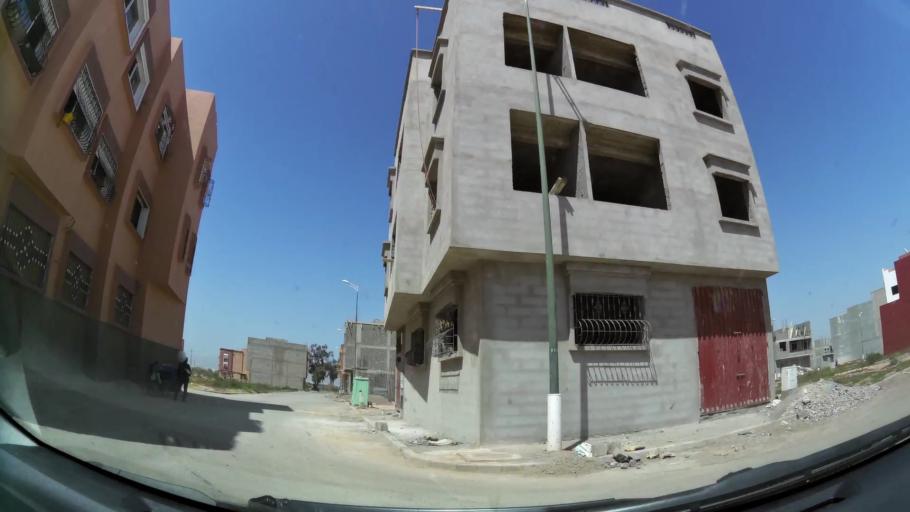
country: MA
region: Souss-Massa-Draa
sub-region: Inezgane-Ait Mellou
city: Inezgane
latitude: 30.3475
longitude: -9.5170
